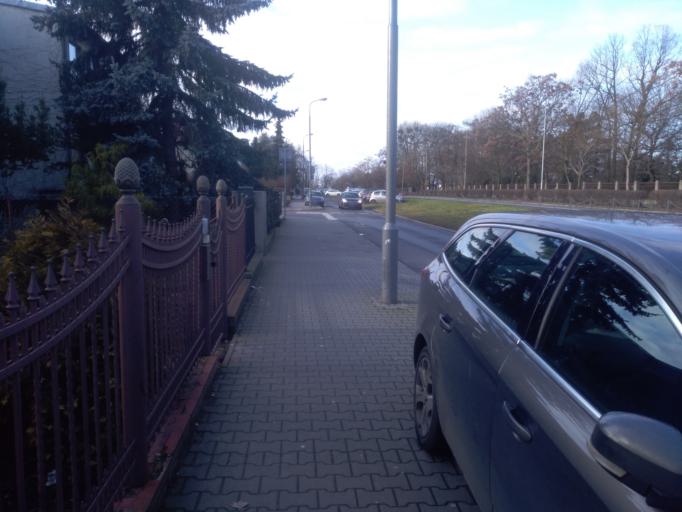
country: PL
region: Greater Poland Voivodeship
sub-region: Poznan
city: Poznan
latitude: 52.4182
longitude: 16.8801
